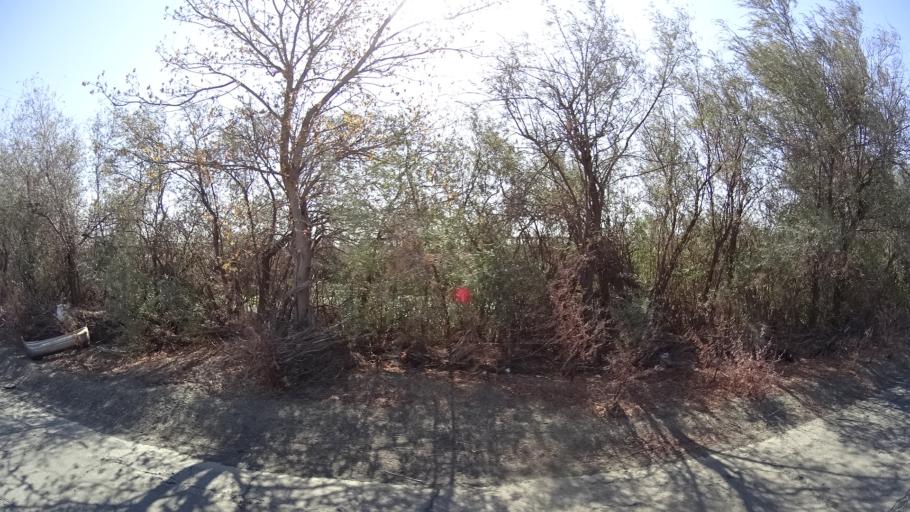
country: US
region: California
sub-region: Yolo County
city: Woodland
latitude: 38.6767
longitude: -121.6598
